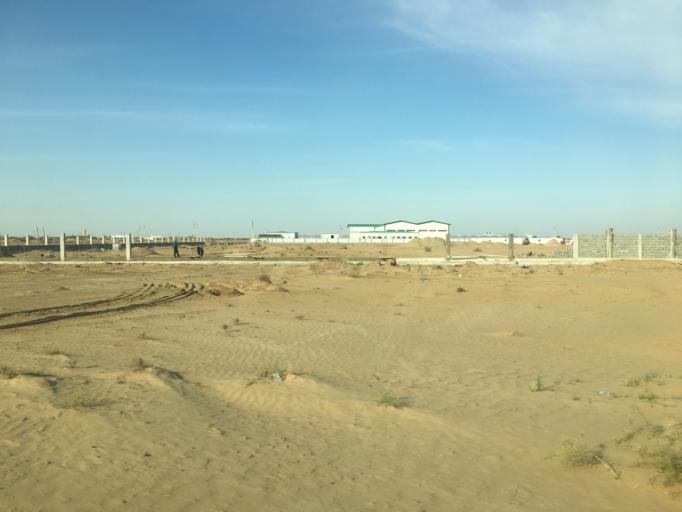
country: TM
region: Mary
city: Mary
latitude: 37.6021
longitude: 61.6125
